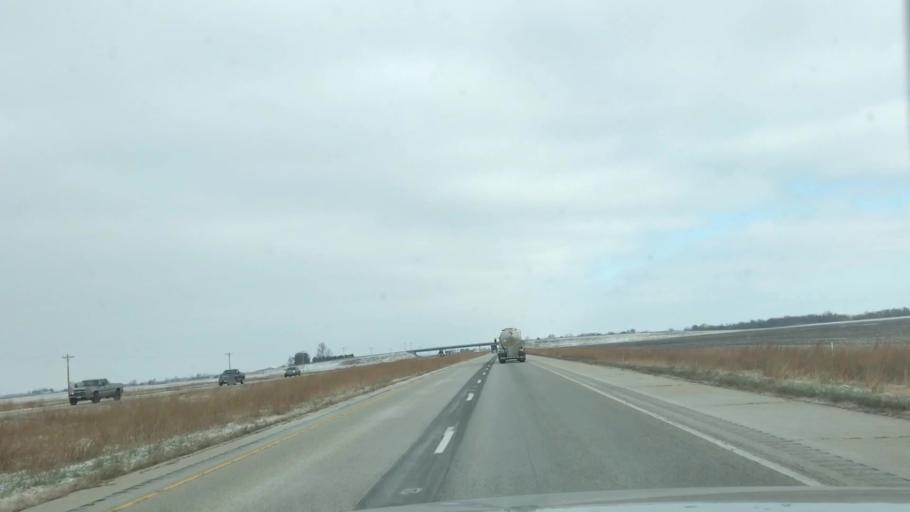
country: US
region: Illinois
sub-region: Sangamon County
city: Divernon
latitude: 39.4942
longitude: -89.6449
